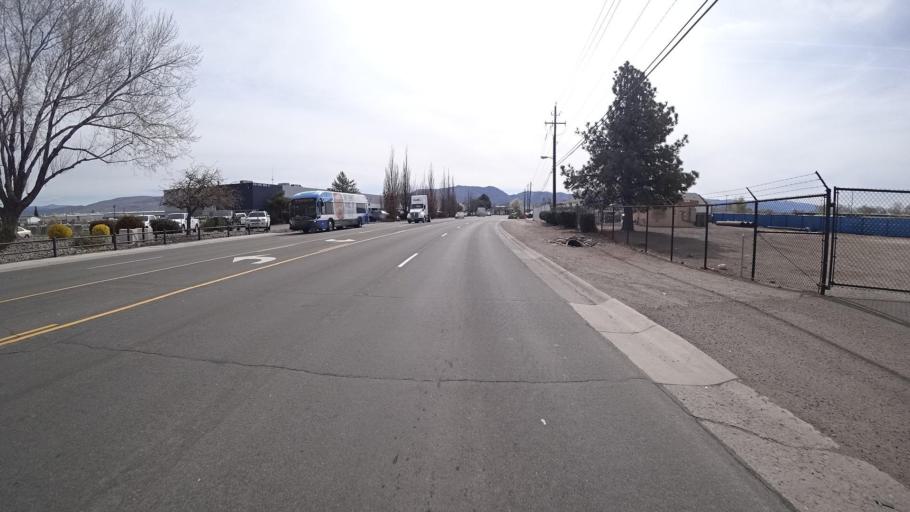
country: US
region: Nevada
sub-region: Washoe County
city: Sparks
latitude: 39.5229
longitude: -119.7574
